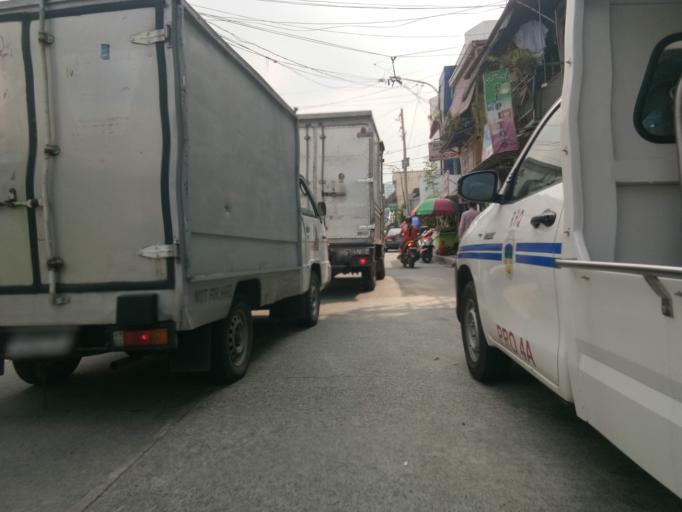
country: PH
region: Metro Manila
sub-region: San Juan
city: San Juan
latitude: 14.6120
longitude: 121.0524
